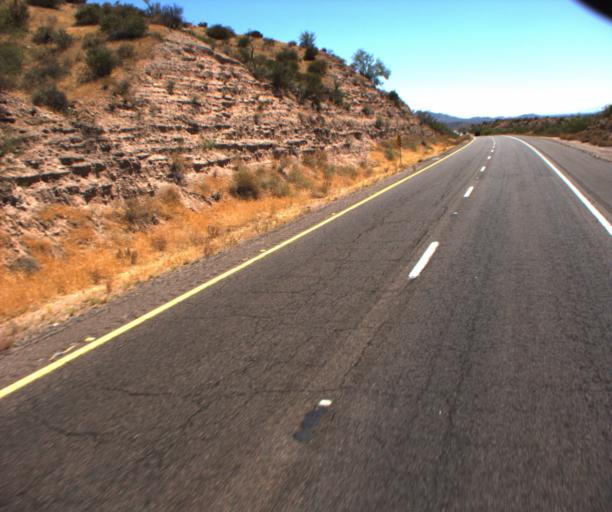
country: US
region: Arizona
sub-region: Maricopa County
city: Fountain Hills
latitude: 33.6167
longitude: -111.5748
